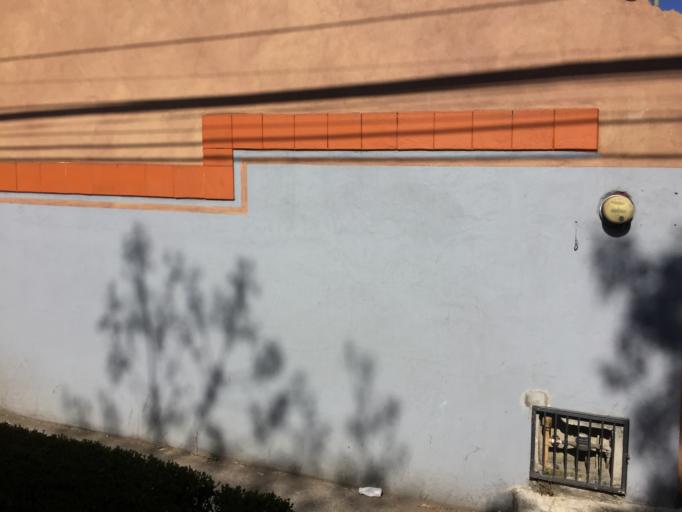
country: MX
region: Veracruz
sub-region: Xalapa
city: Xalapa de Enriquez
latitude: 19.5408
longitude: -96.9216
